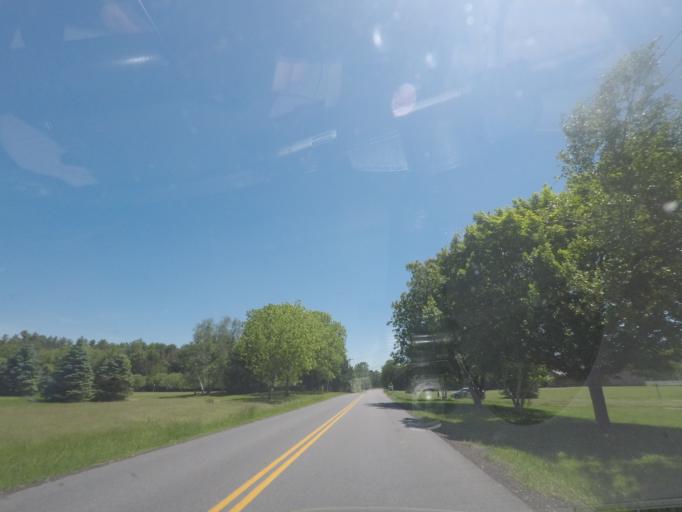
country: US
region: New York
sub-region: Saratoga County
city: Country Knolls
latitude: 42.9441
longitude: -73.7537
